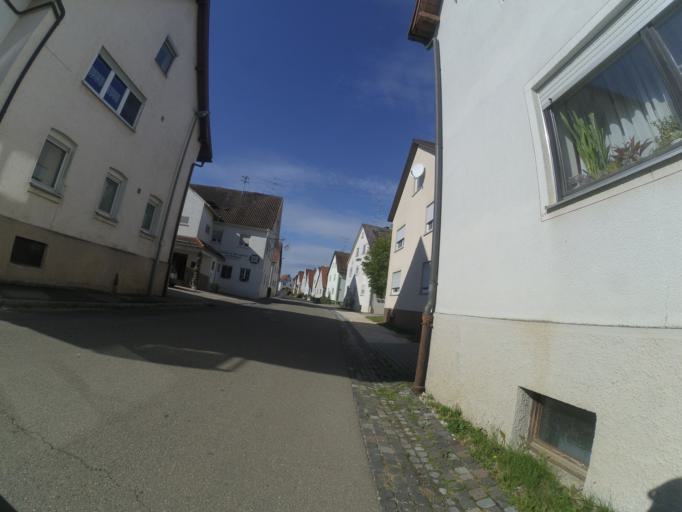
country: DE
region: Baden-Wuerttemberg
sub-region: Tuebingen Region
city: Weidenstetten
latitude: 48.5530
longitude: 9.9953
